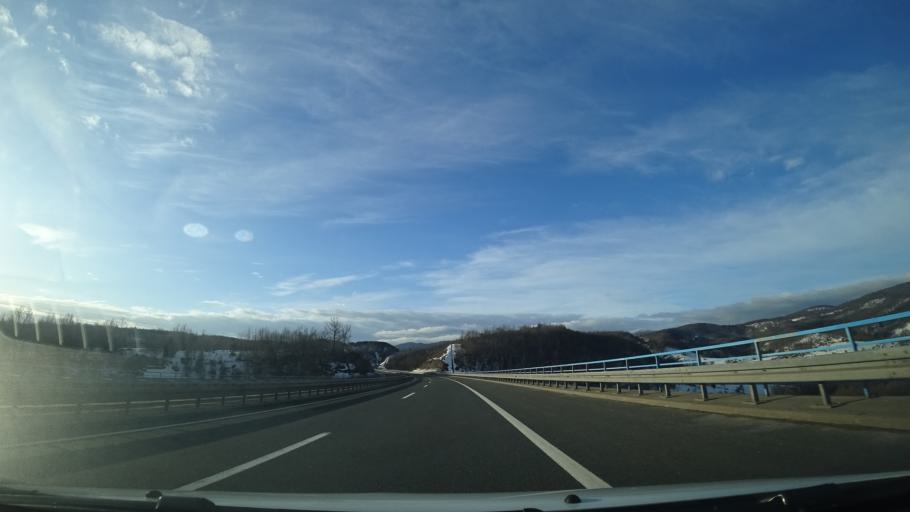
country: HR
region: Karlovacka
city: Ostarije
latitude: 45.1548
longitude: 15.2722
